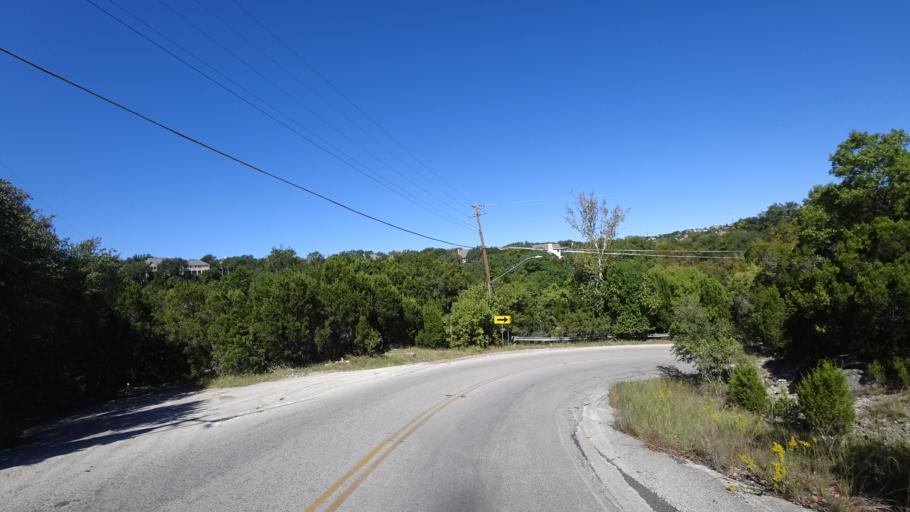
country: US
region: Texas
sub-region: Travis County
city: West Lake Hills
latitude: 30.3362
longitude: -97.7771
